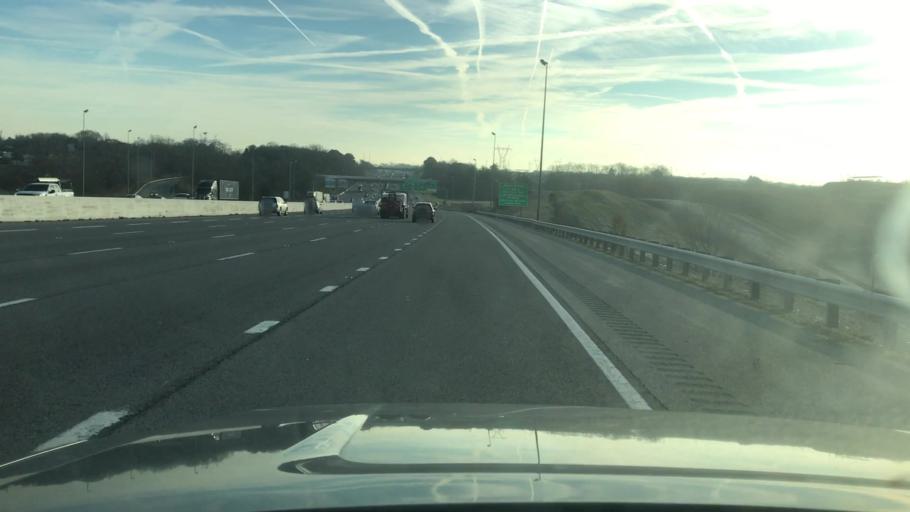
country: US
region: Tennessee
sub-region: Davidson County
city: Nashville
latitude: 36.1422
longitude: -86.6806
